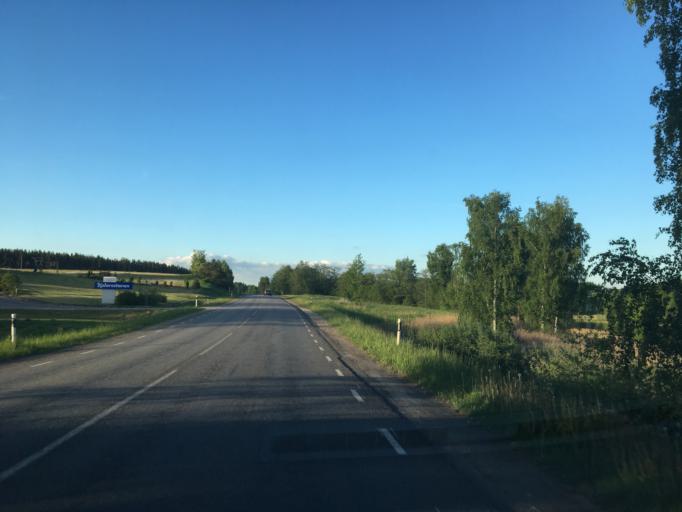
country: EE
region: Tartu
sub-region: Noo vald
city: Noo
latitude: 58.2016
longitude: 26.5740
